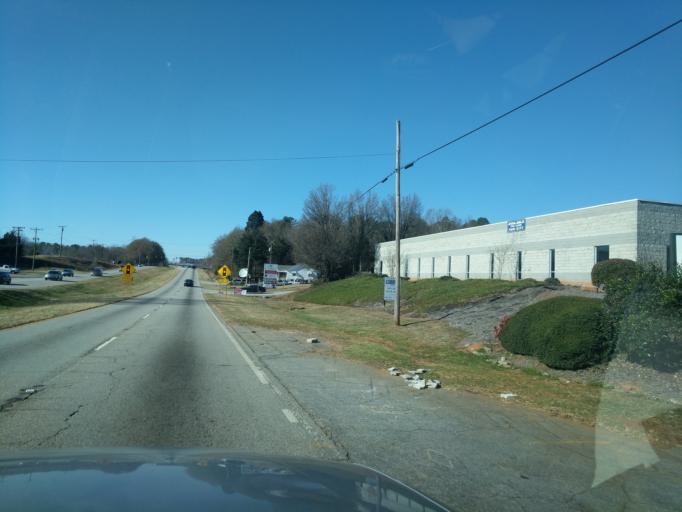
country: US
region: South Carolina
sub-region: Anderson County
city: Powdersville
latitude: 34.8301
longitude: -82.5139
